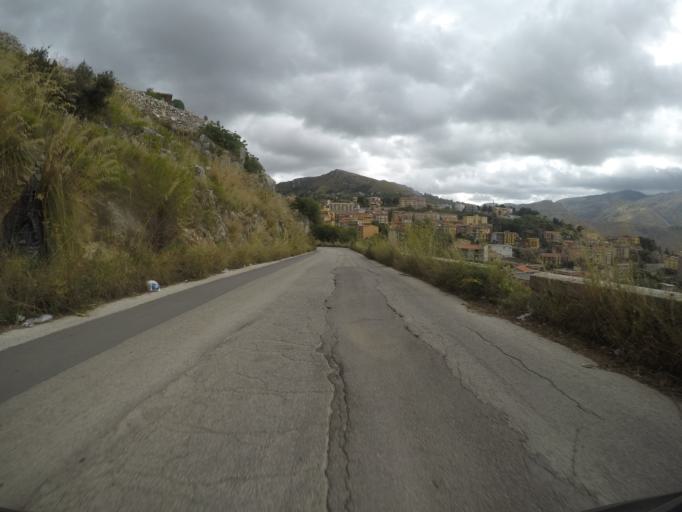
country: IT
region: Sicily
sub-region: Palermo
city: Montelepre
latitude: 38.0926
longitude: 13.1754
